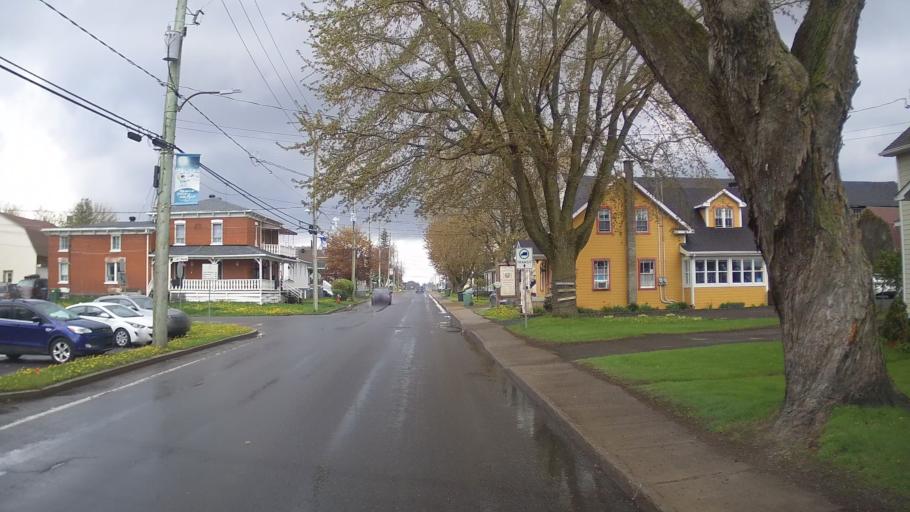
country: CA
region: Quebec
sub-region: Monteregie
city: Farnham
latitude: 45.3229
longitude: -73.0646
